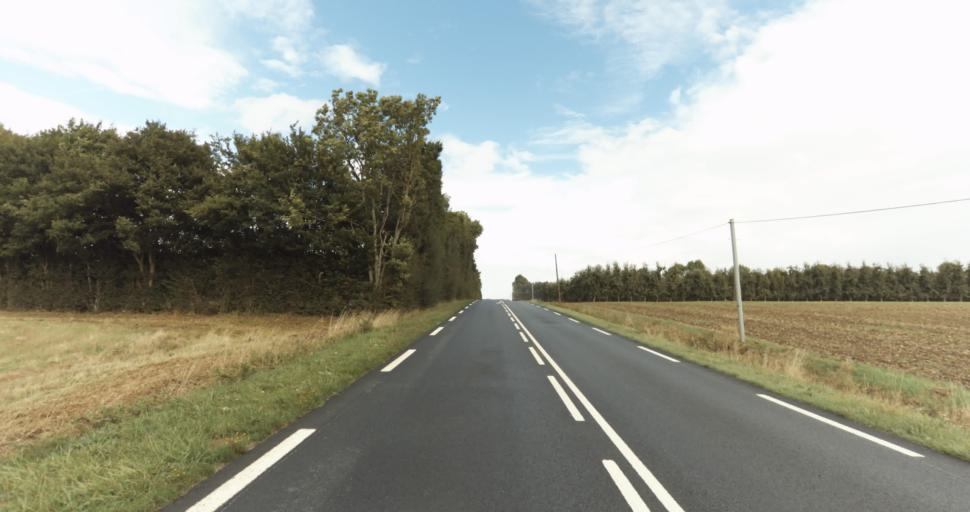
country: FR
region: Lower Normandy
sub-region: Departement de l'Orne
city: Sainte-Gauburge-Sainte-Colombe
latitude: 48.7073
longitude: 0.3838
